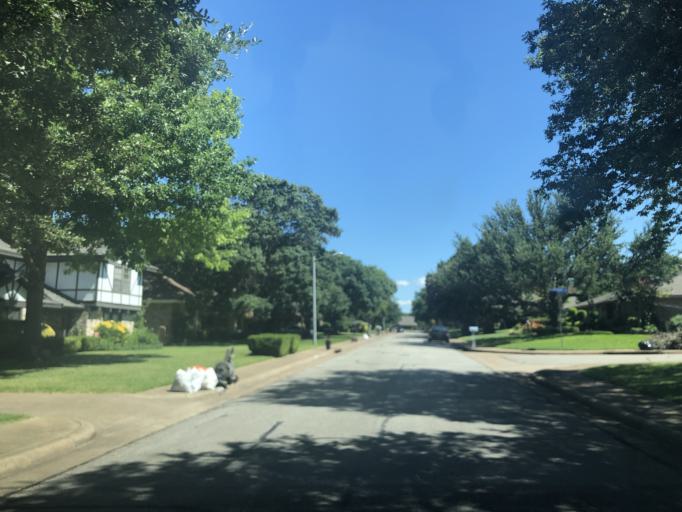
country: US
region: Texas
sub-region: Dallas County
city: Duncanville
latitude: 32.6442
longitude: -96.9383
